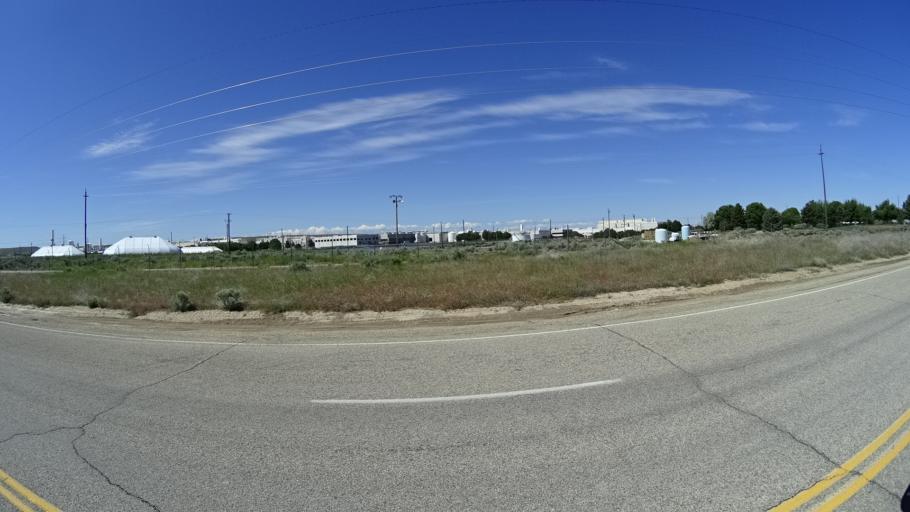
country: US
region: Idaho
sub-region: Ada County
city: Boise
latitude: 43.5320
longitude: -116.1402
